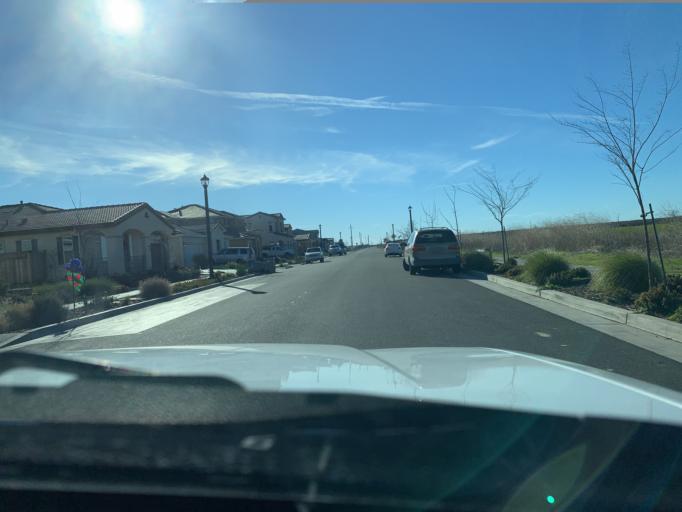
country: US
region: California
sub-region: Yolo County
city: Woodland
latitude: 38.6467
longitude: -121.7474
